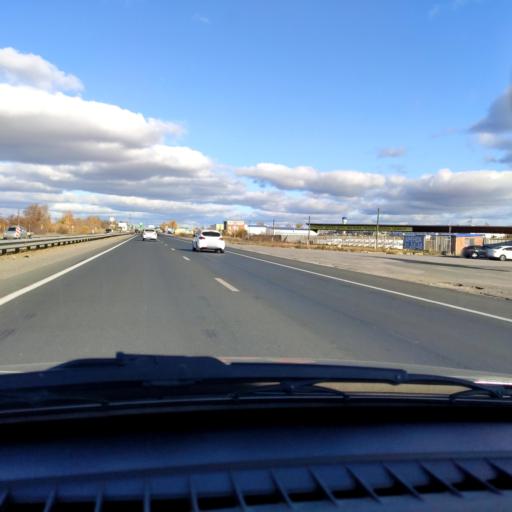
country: RU
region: Samara
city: Tol'yatti
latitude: 53.5752
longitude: 49.3943
